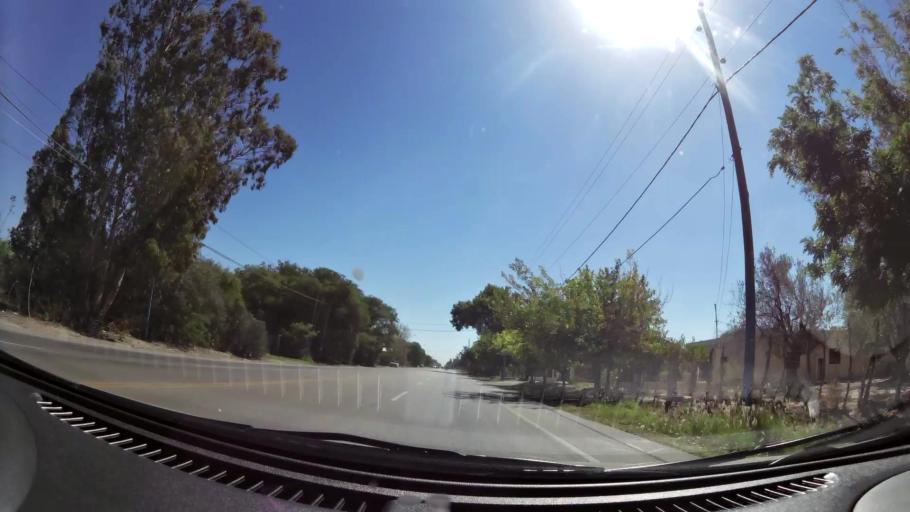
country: AR
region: San Juan
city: Villa Aberastain
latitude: -31.6157
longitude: -68.5482
